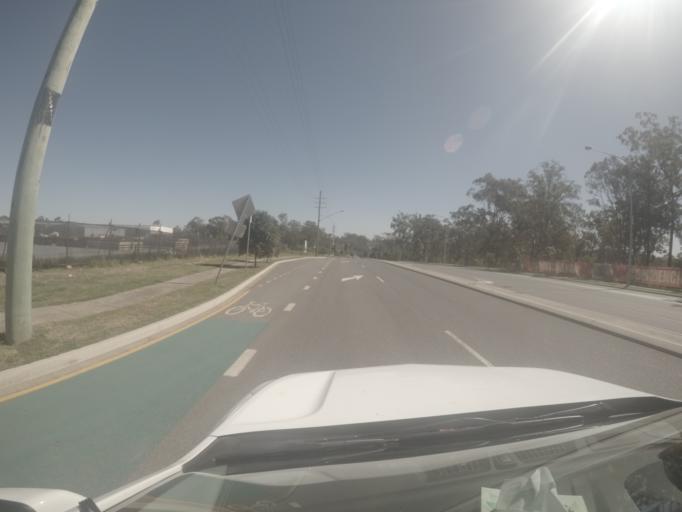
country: AU
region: Queensland
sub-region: Brisbane
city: Wacol
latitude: -27.5849
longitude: 152.9413
